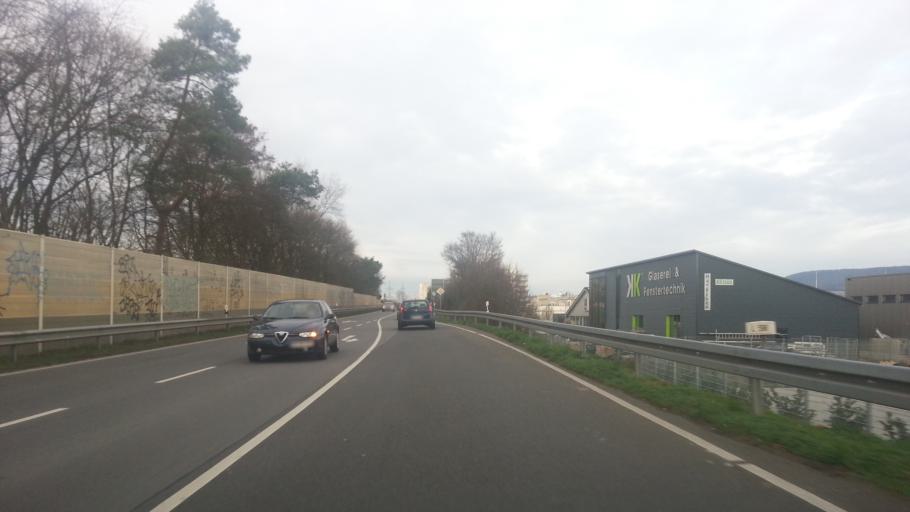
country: DE
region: Baden-Wuerttemberg
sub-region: Karlsruhe Region
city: Sandhausen
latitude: 49.3390
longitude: 8.6661
